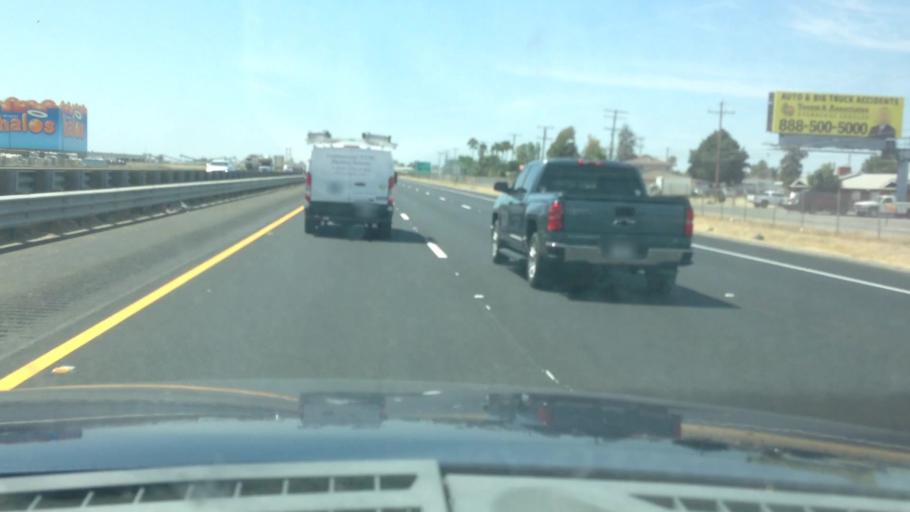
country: US
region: California
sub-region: Kern County
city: Delano
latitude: 35.7380
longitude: -119.2412
